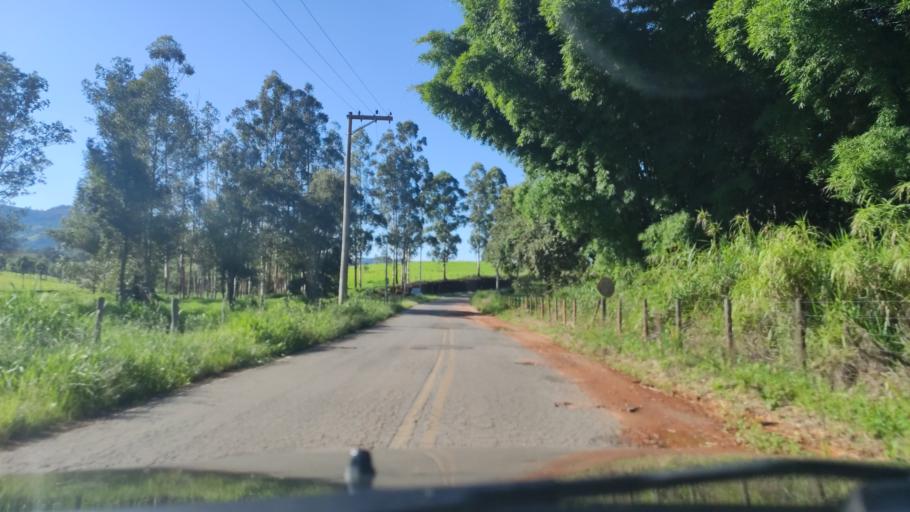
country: BR
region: Sao Paulo
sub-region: Serra Negra
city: Serra Negra
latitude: -22.5741
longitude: -46.6214
